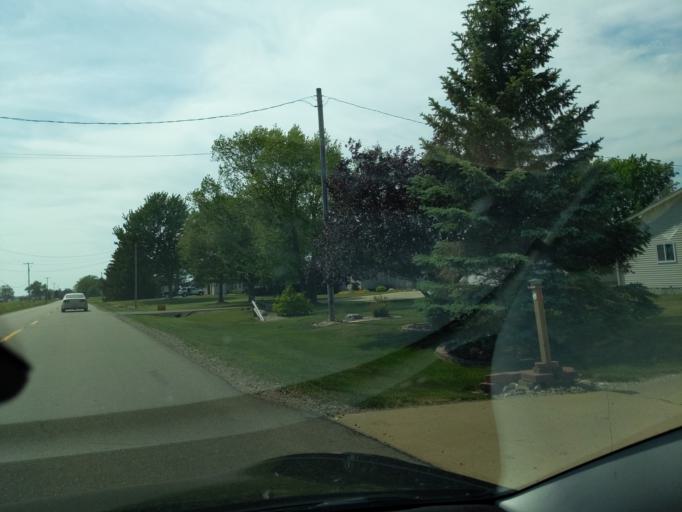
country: US
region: Michigan
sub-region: Eaton County
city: Grand Ledge
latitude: 42.7118
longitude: -84.7423
